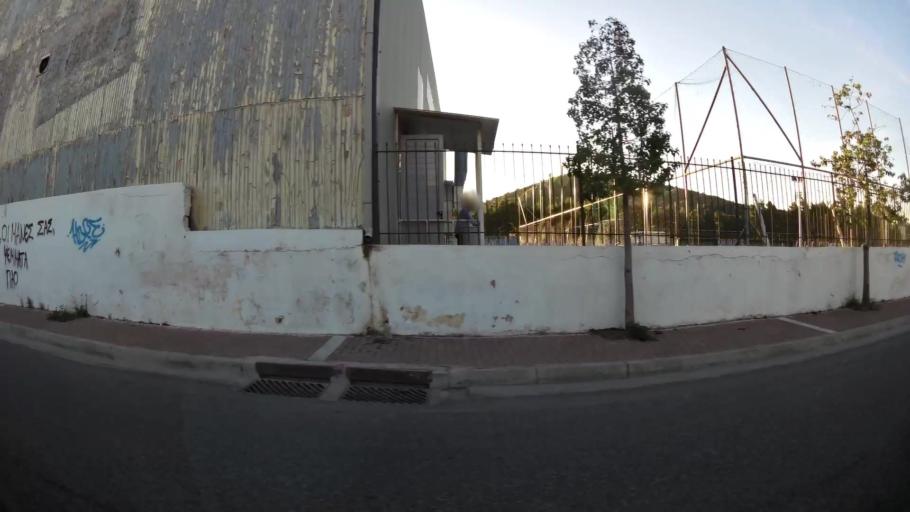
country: GR
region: Attica
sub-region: Nomarchia Anatolikis Attikis
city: Spata
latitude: 37.9669
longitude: 23.9061
